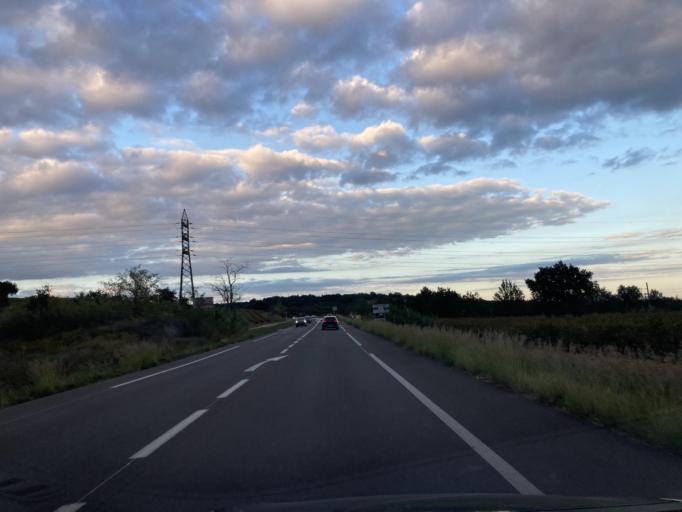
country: FR
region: Languedoc-Roussillon
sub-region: Departement des Pyrenees-Orientales
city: Banyuls-dels-Aspres
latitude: 42.5503
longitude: 2.8569
